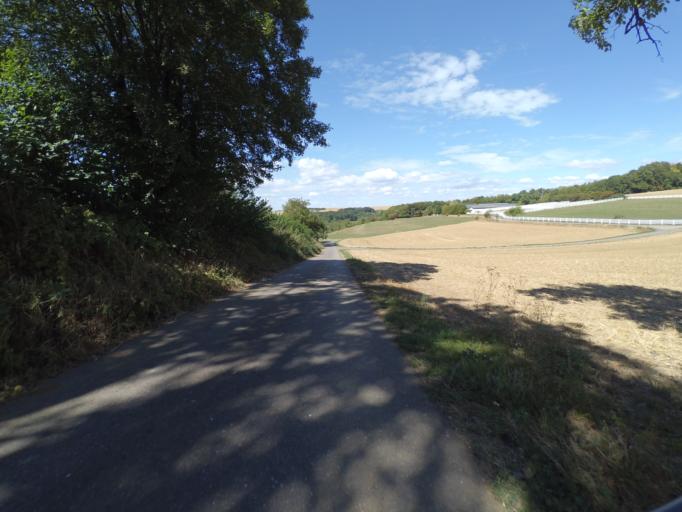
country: DE
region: Rheinland-Pfalz
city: Merzkirchen
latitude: 49.5956
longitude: 6.4930
